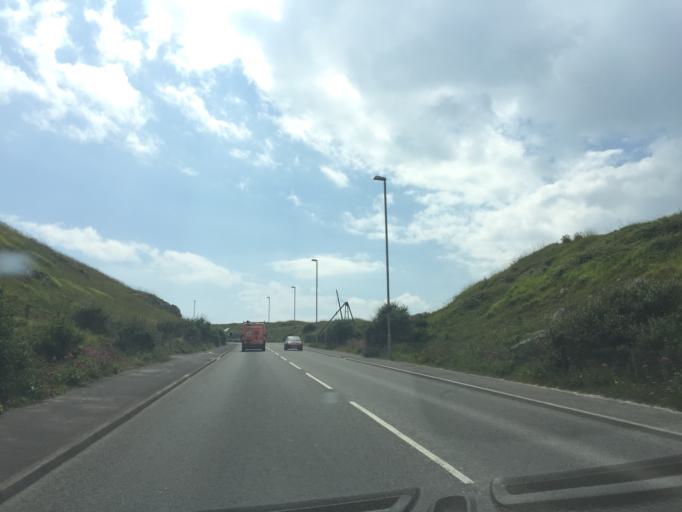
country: GB
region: England
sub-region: Dorset
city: Fortuneswell
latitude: 50.5558
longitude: -2.4435
